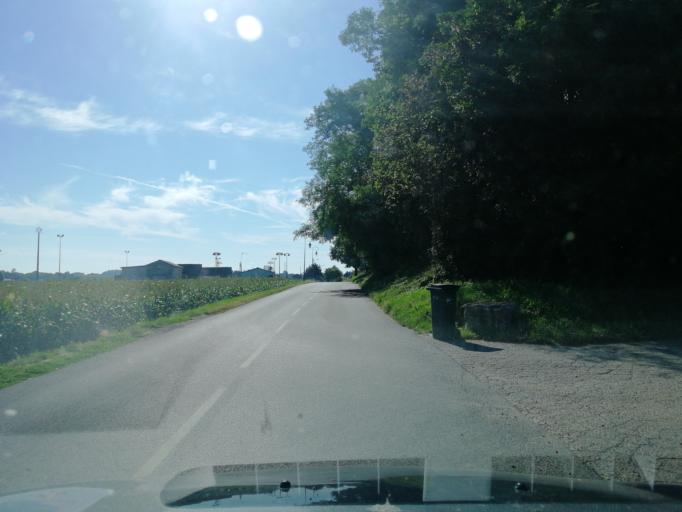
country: FR
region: Rhone-Alpes
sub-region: Departement du Rhone
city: Sathonay-Village
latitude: 45.8379
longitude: 4.8688
